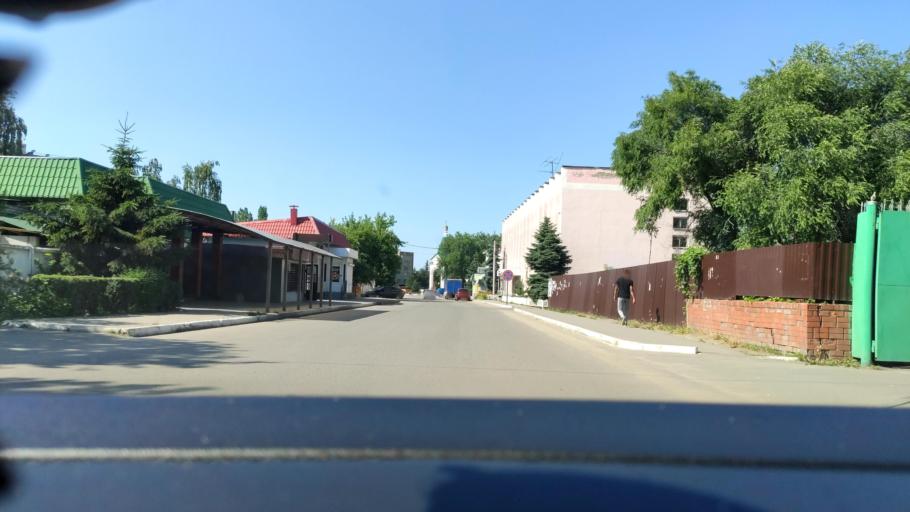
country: RU
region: Voronezj
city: Novaya Usman'
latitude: 51.6422
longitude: 39.4116
